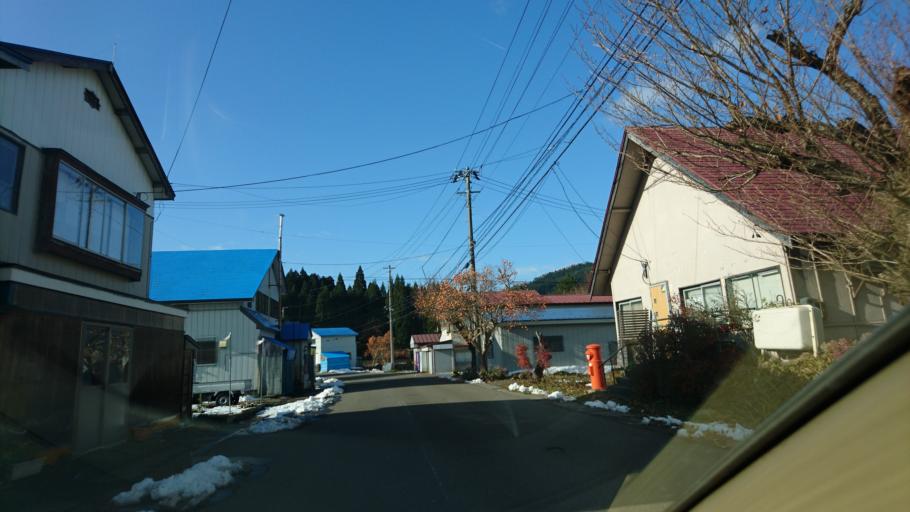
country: JP
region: Iwate
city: Kitakami
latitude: 39.2963
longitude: 140.8355
